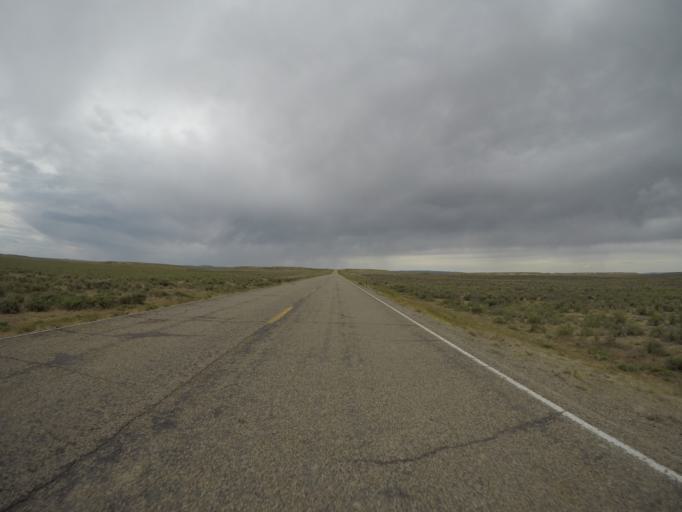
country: US
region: Wyoming
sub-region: Lincoln County
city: Kemmerer
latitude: 41.9636
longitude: -110.1436
